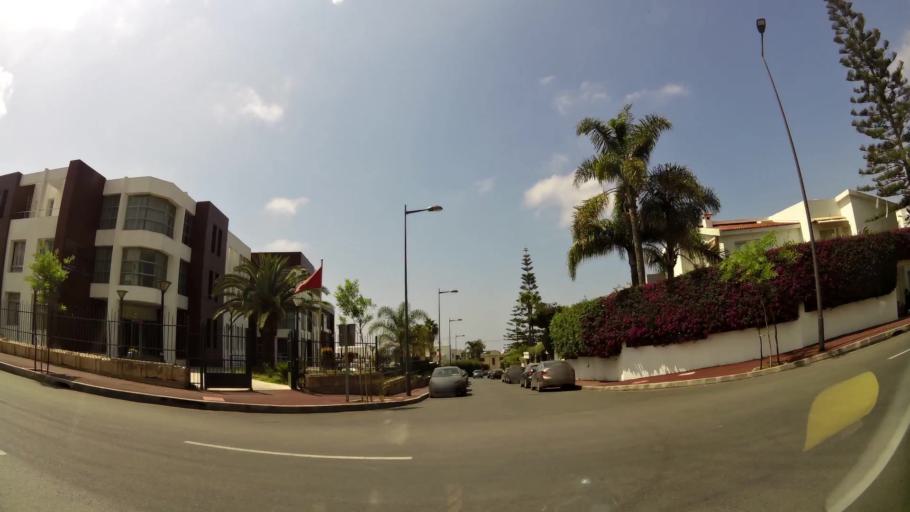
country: MA
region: Rabat-Sale-Zemmour-Zaer
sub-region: Skhirate-Temara
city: Temara
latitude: 33.9634
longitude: -6.8765
